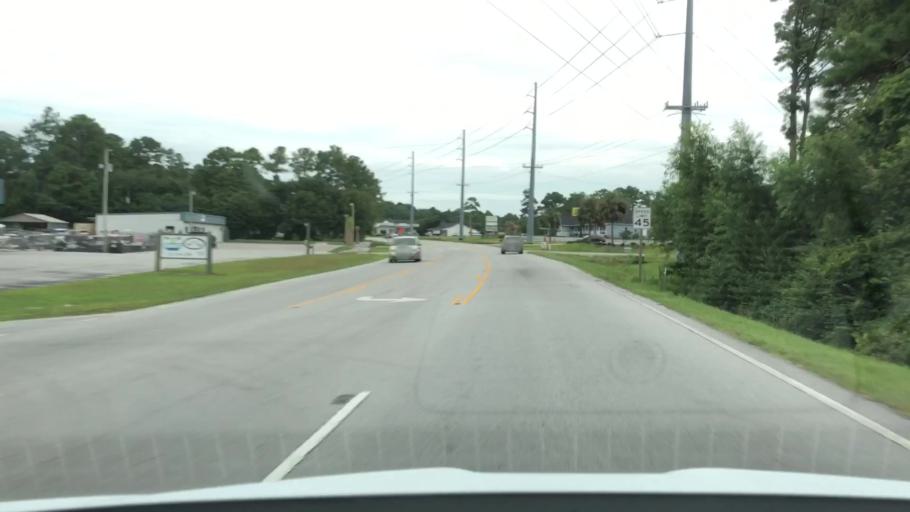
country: US
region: North Carolina
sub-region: Carteret County
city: Cape Carteret
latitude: 34.7131
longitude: -77.0678
